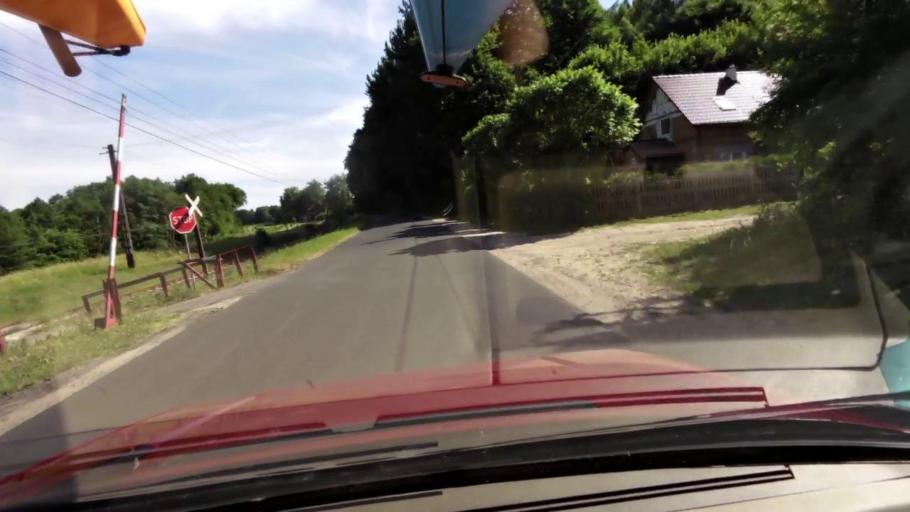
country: PL
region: Pomeranian Voivodeship
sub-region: Powiat slupski
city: Kepice
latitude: 54.1955
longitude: 16.8872
